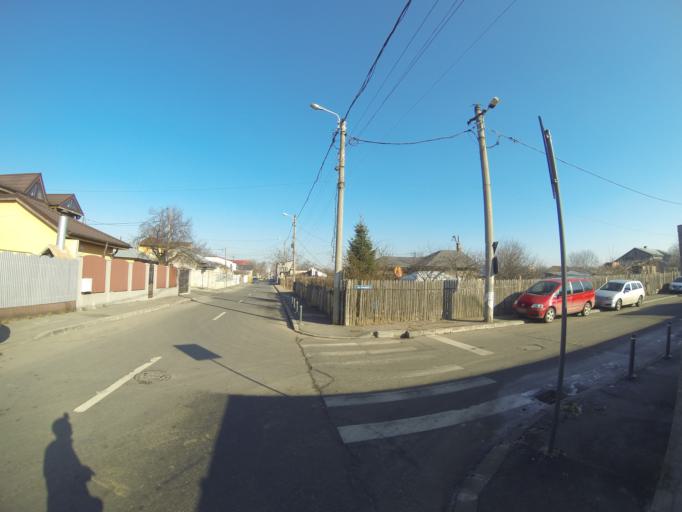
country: RO
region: Ilfov
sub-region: Comuna Magurele
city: Magurele
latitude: 44.3943
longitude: 26.0578
